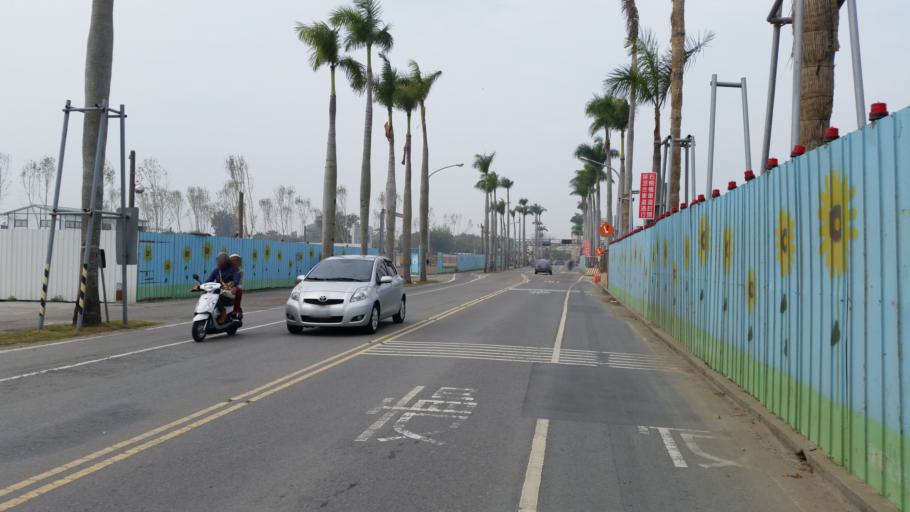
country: TW
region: Taiwan
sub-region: Tainan
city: Tainan
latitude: 22.9648
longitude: 120.2191
